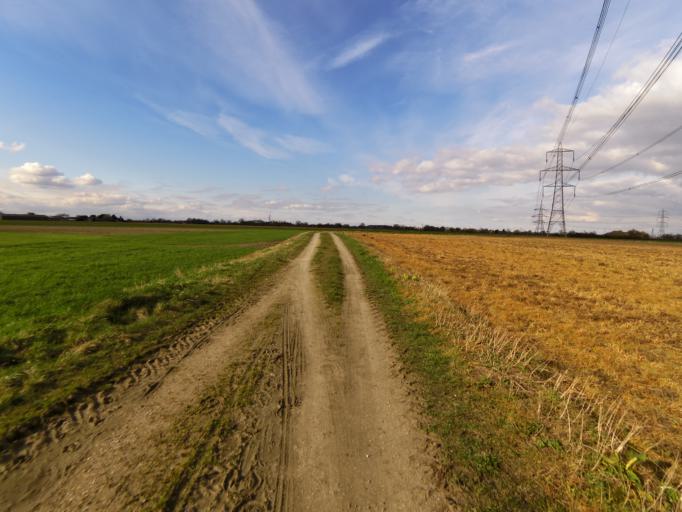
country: GB
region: England
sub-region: East Riding of Yorkshire
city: Pollington
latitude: 53.6538
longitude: -1.0656
